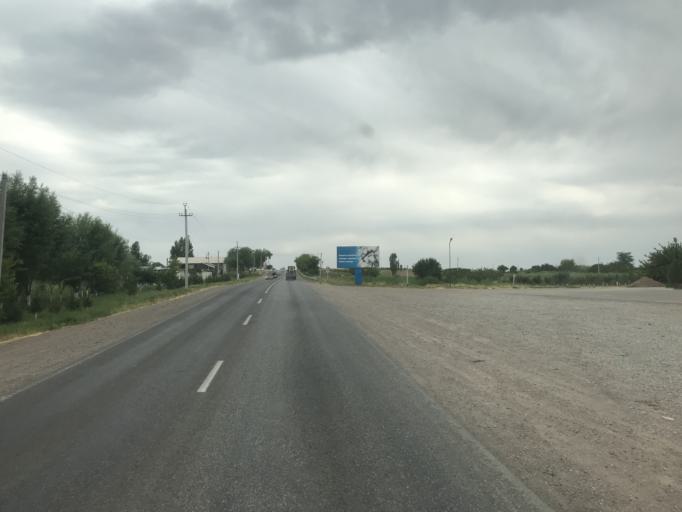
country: UZ
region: Toshkent
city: Salor
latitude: 41.4971
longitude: 69.3420
